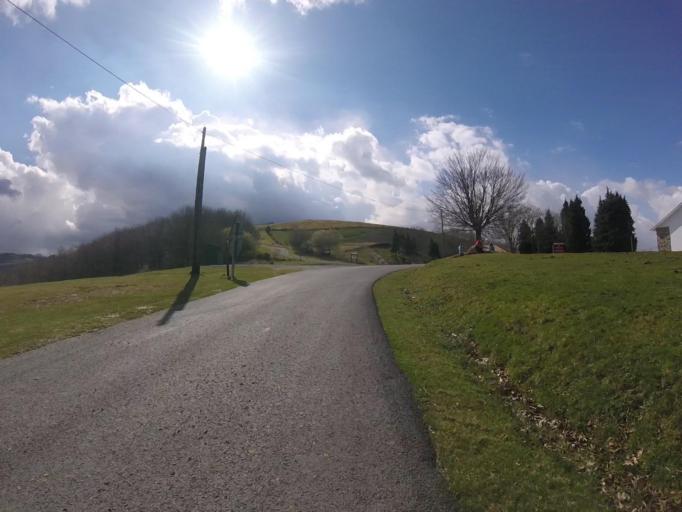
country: ES
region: Navarre
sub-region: Provincia de Navarra
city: Etxalar
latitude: 43.2610
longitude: -1.6189
